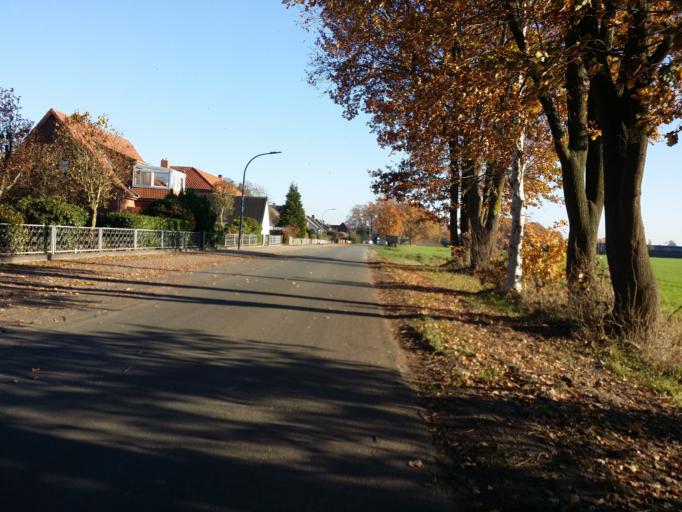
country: DE
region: Lower Saxony
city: Ottersberg
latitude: 53.0622
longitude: 9.0952
